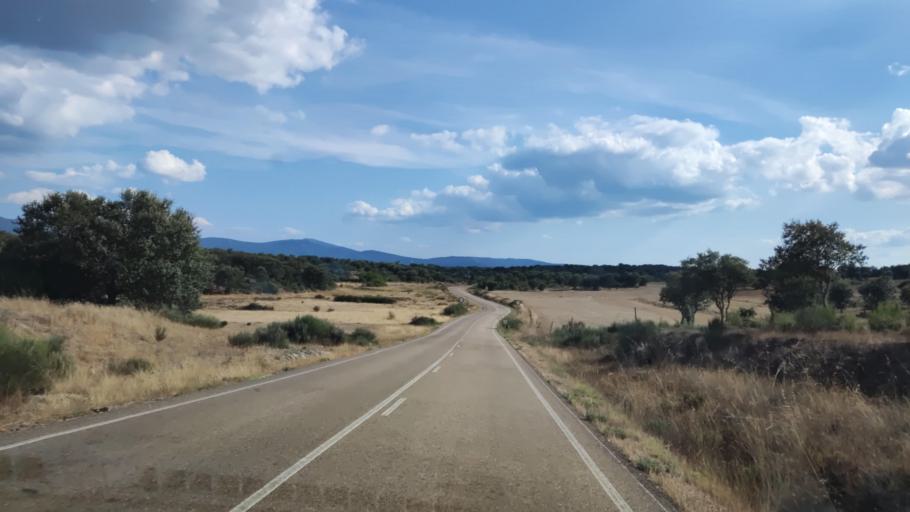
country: ES
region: Castille and Leon
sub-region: Provincia de Salamanca
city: Martiago
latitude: 40.4772
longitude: -6.4906
